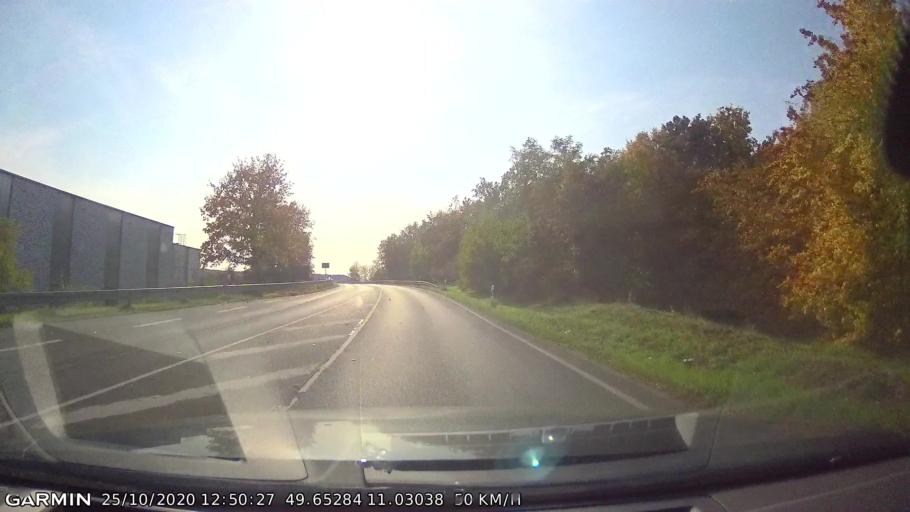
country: DE
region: Bavaria
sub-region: Regierungsbezirk Mittelfranken
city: Baiersdorf
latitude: 49.6526
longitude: 11.0303
